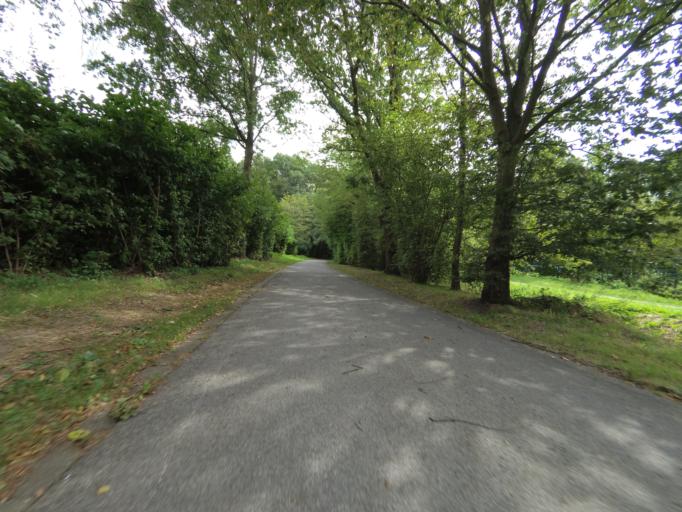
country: DE
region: North Rhine-Westphalia
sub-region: Regierungsbezirk Munster
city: Ahaus
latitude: 52.0801
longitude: 6.9891
